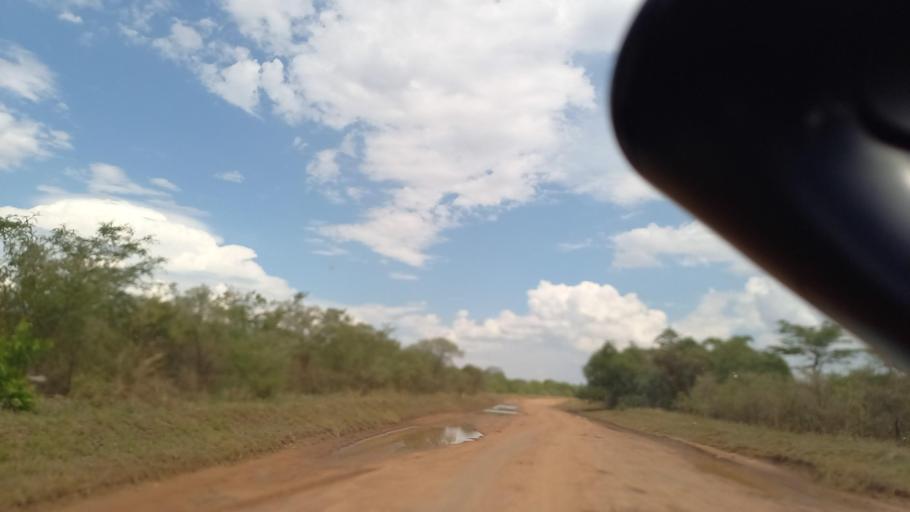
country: ZM
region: Southern
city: Nakambala
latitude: -16.0505
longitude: 27.9832
